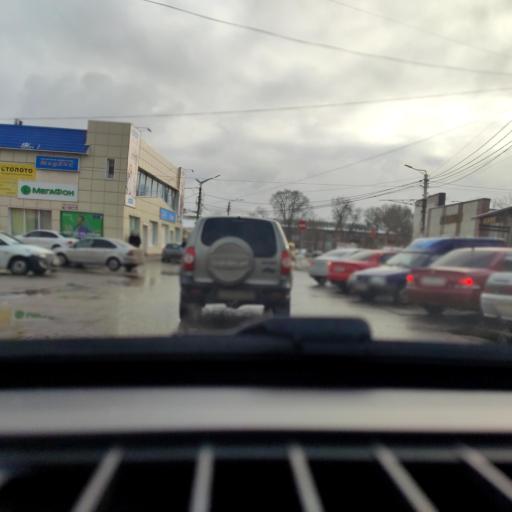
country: RU
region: Voronezj
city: Semiluki
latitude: 51.6831
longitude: 39.0353
